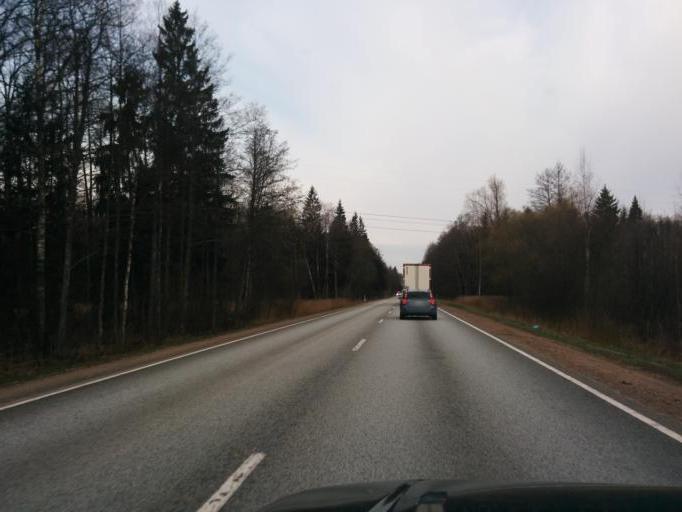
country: LV
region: Kekava
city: Balozi
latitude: 56.8205
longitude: 24.0944
